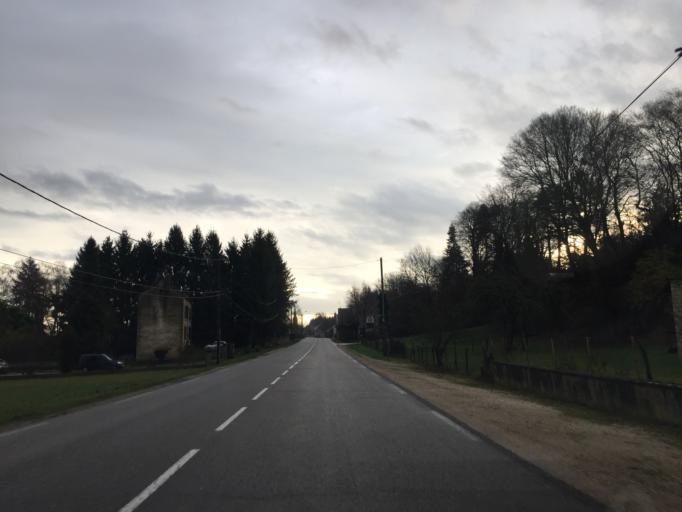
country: FR
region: Franche-Comte
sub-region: Departement du Jura
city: Mont-sous-Vaudrey
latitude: 46.9969
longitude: 5.5424
